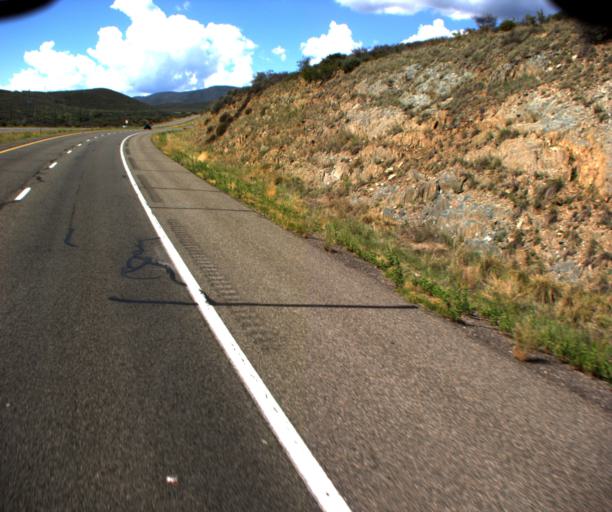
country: US
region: Arizona
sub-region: Yavapai County
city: Dewey-Humboldt
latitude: 34.4719
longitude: -112.2636
